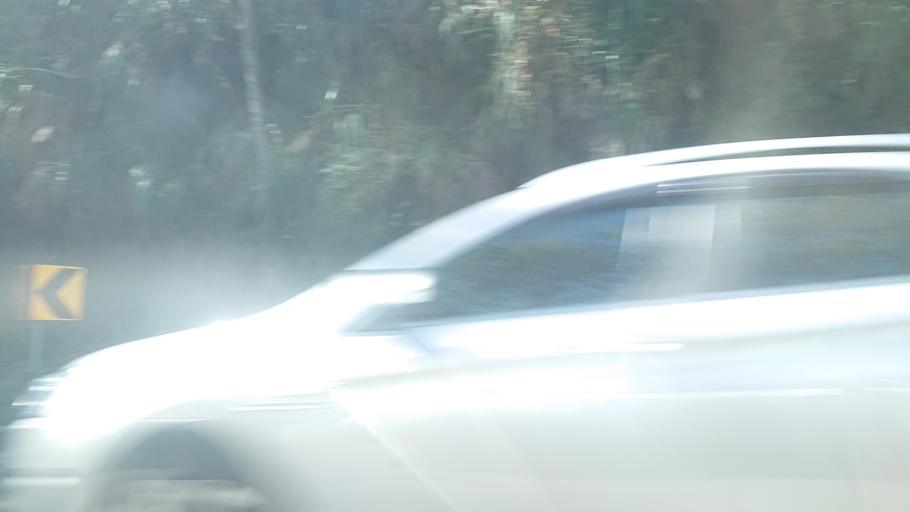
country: TW
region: Taiwan
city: Lugu
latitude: 23.4816
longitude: 120.8327
